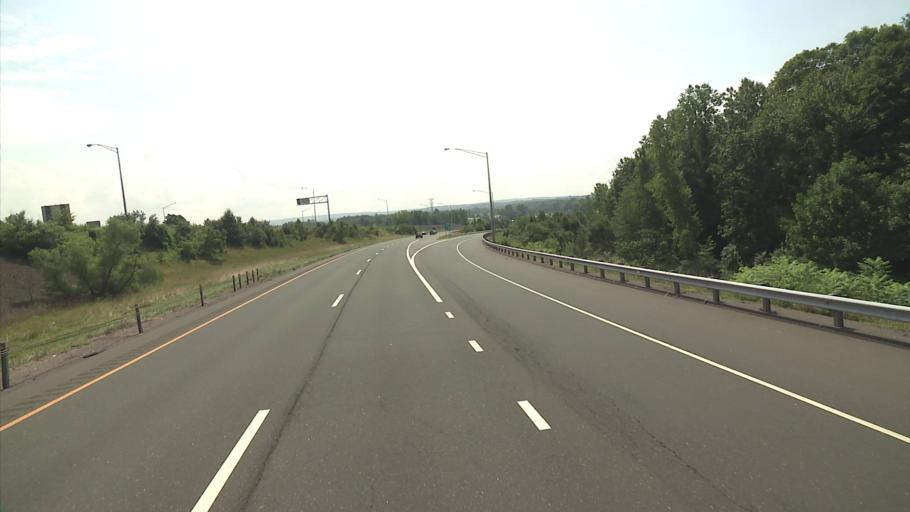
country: US
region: Connecticut
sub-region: Hartford County
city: East Hartford
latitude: 41.7724
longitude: -72.5828
